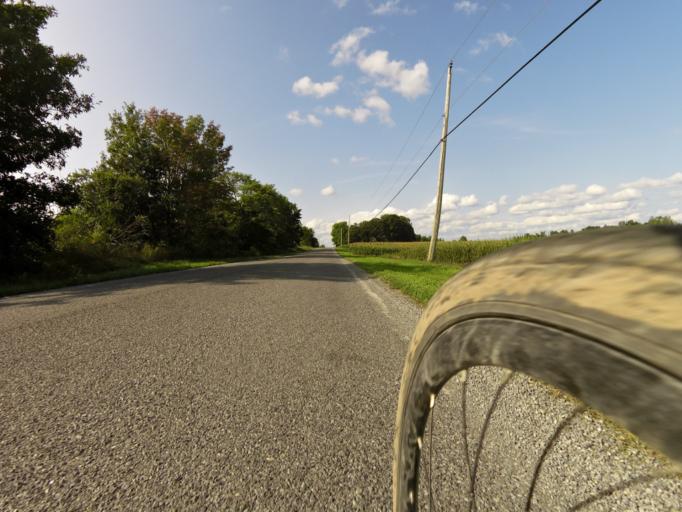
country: CA
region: Ontario
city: Kingston
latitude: 44.3968
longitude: -76.5961
